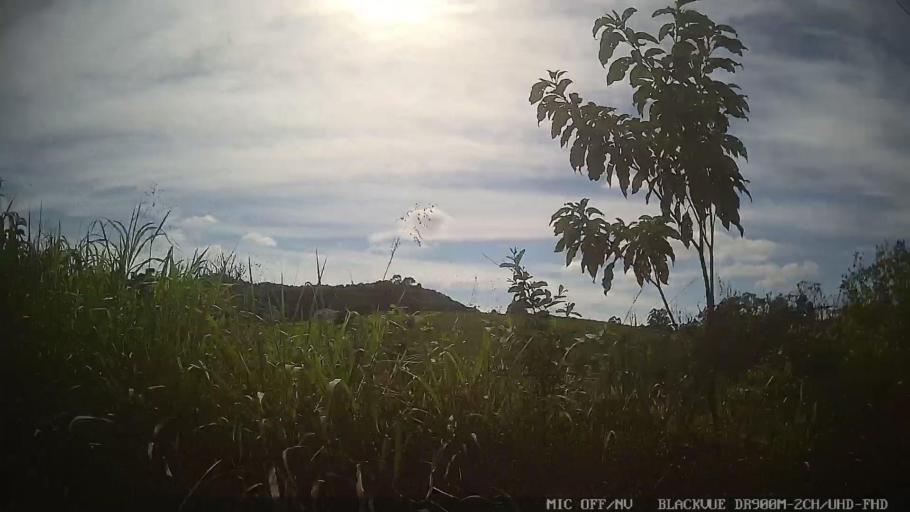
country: BR
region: Sao Paulo
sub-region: Jarinu
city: Jarinu
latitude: -23.0247
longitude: -46.6371
